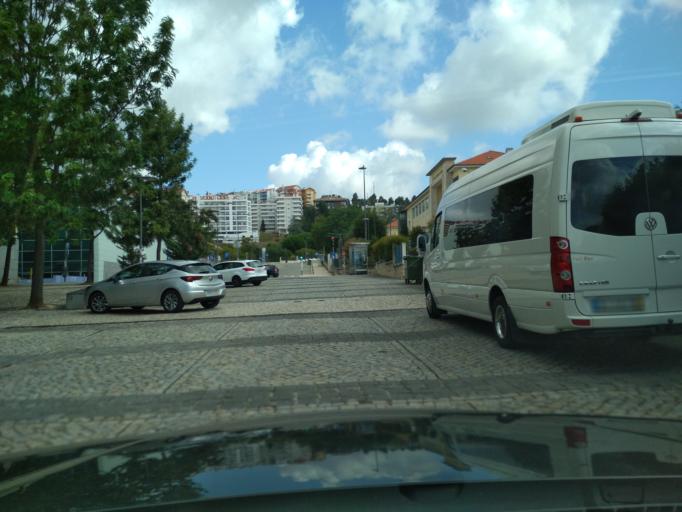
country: PT
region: Coimbra
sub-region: Coimbra
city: Coimbra
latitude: 40.2044
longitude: -8.4064
